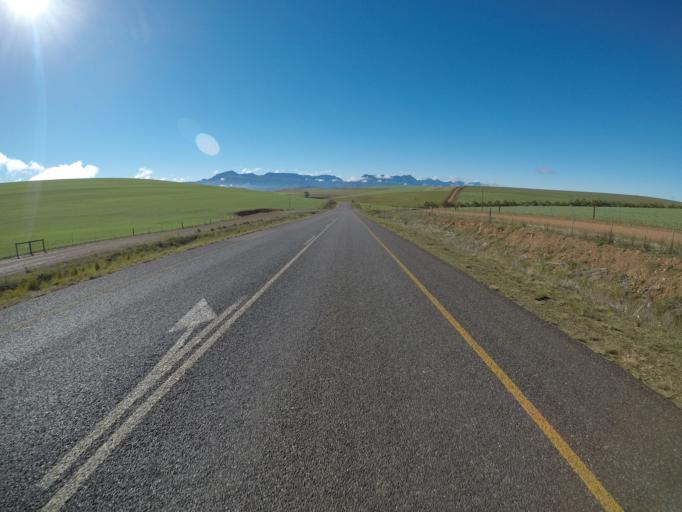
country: ZA
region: Western Cape
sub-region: Overberg District Municipality
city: Caledon
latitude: -34.1399
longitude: 19.5039
